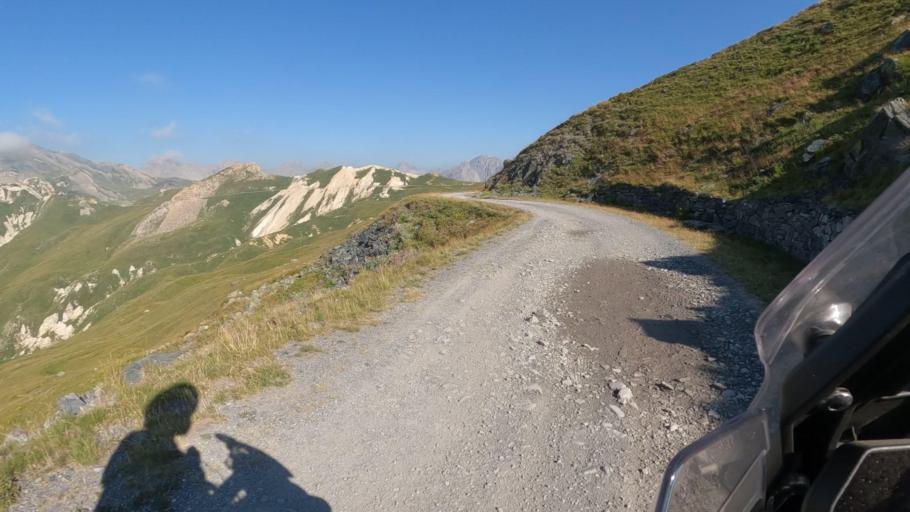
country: IT
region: Piedmont
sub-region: Provincia di Cuneo
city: Sambuco
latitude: 44.3847
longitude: 7.0739
